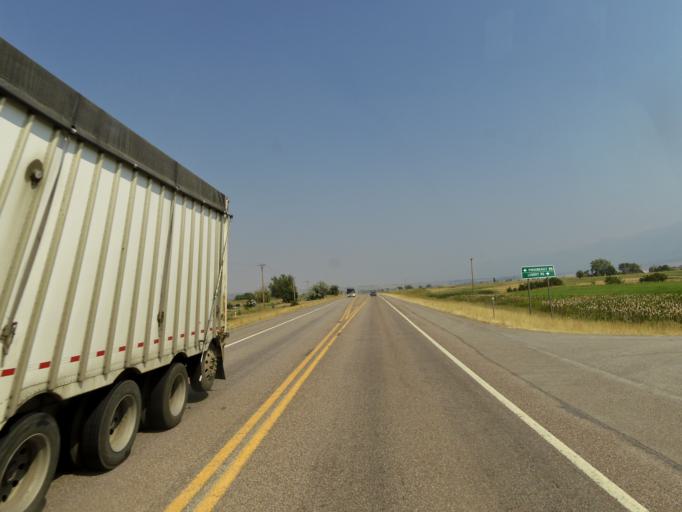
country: US
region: Montana
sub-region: Lake County
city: Ronan
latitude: 47.3519
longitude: -114.0968
